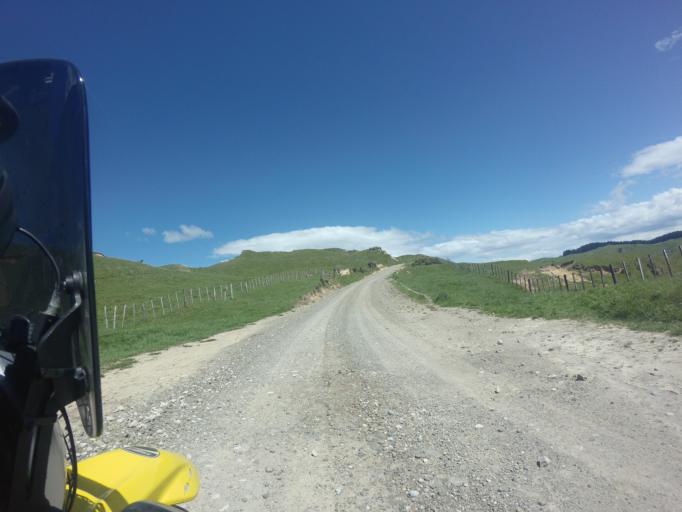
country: NZ
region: Hawke's Bay
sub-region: Wairoa District
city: Wairoa
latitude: -38.9500
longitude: 177.7239
